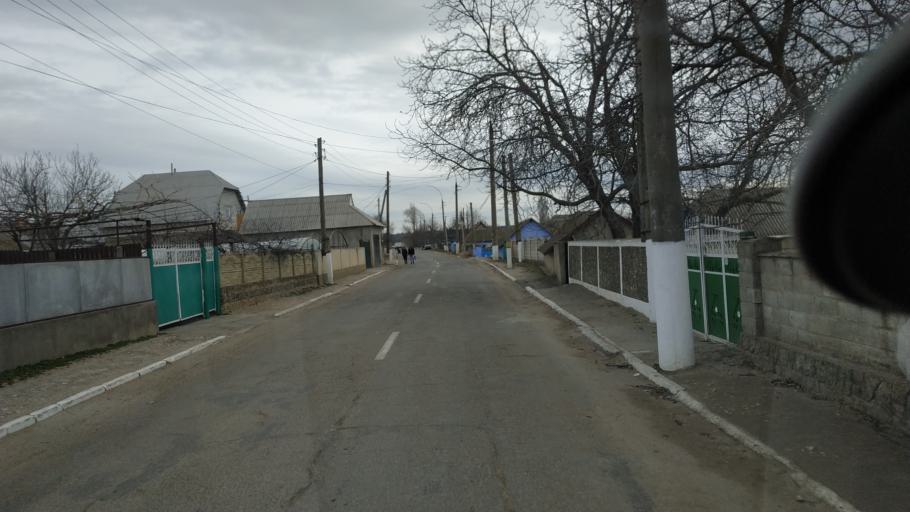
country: MD
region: Telenesti
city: Cocieri
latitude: 47.3433
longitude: 29.1152
